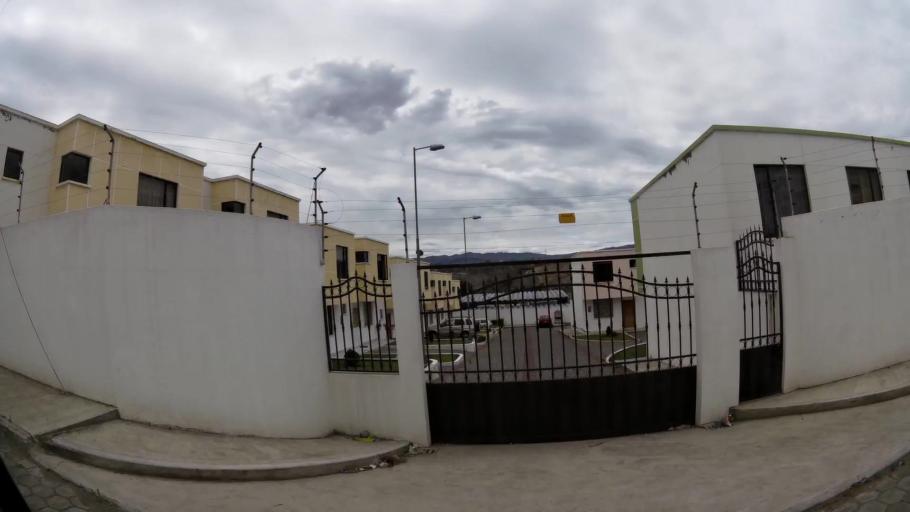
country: EC
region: Cotopaxi
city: Latacunga
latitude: -0.9599
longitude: -78.6109
